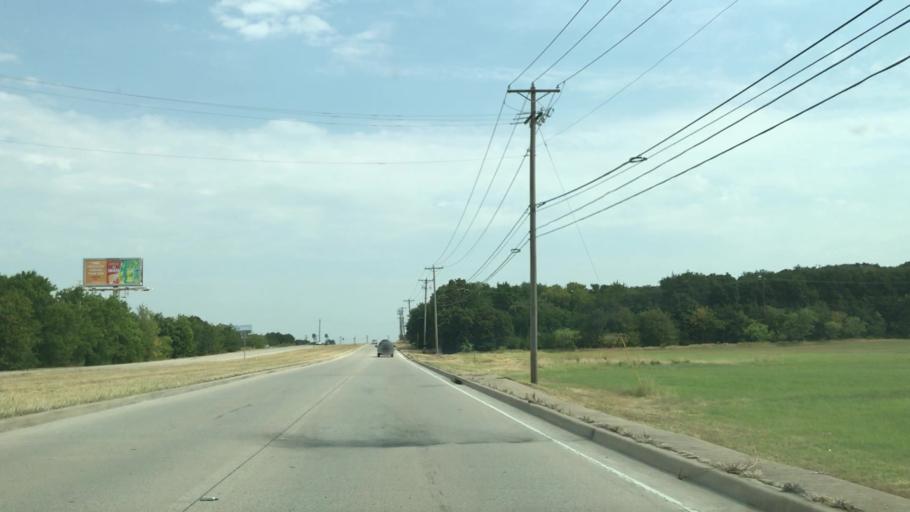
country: US
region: Texas
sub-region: Tarrant County
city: Keller
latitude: 32.9500
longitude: -97.2540
